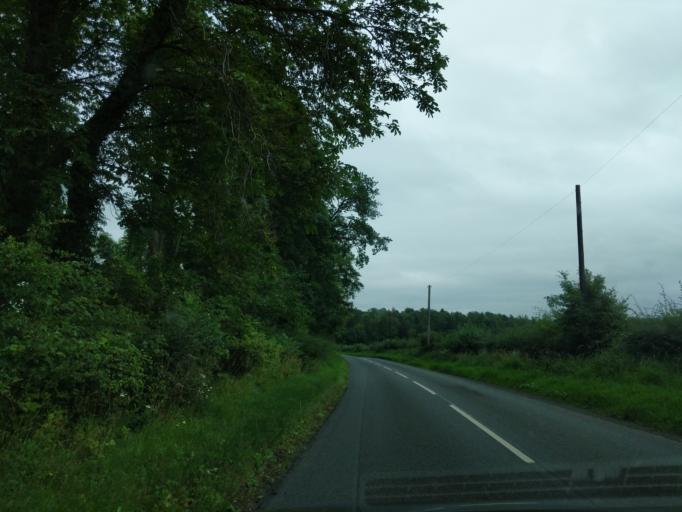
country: GB
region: Scotland
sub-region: East Lothian
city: Pencaitland
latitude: 55.8967
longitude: -2.8758
